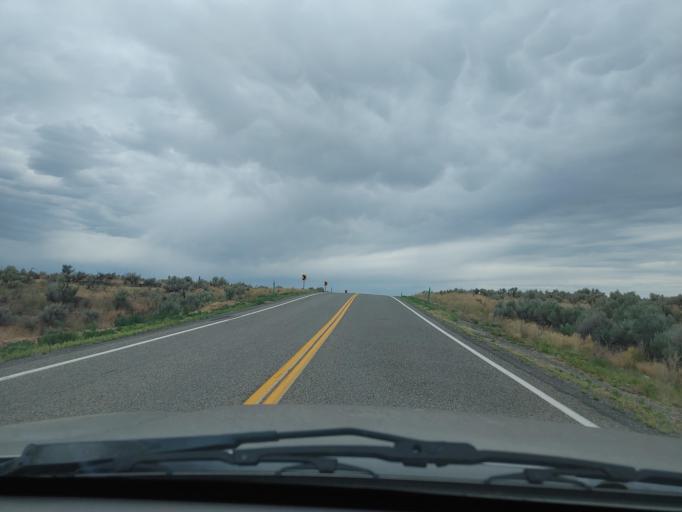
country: US
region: Idaho
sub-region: Lincoln County
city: Shoshone
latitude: 43.0814
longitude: -114.1006
